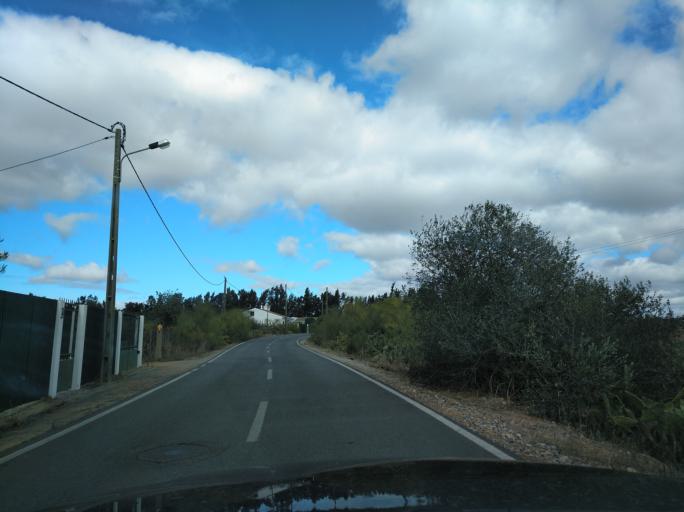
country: PT
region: Faro
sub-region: Vila Real de Santo Antonio
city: Monte Gordo
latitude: 37.1840
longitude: -7.4950
